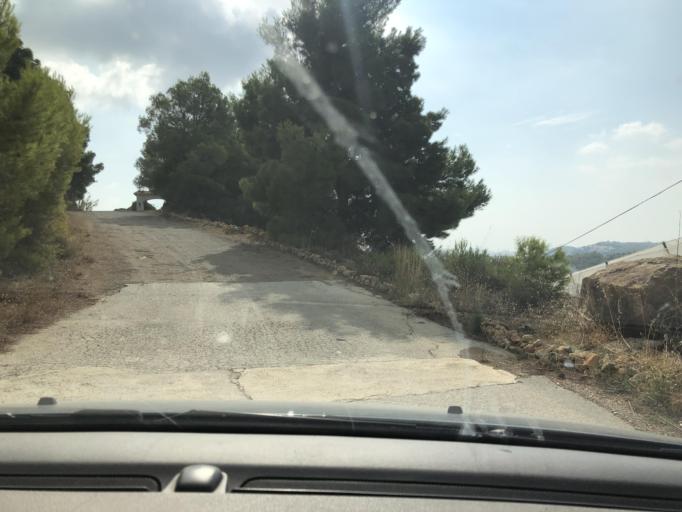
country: ES
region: Valencia
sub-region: Provincia de Alicante
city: Callosa d'En Sarria
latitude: 38.6334
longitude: -0.1124
